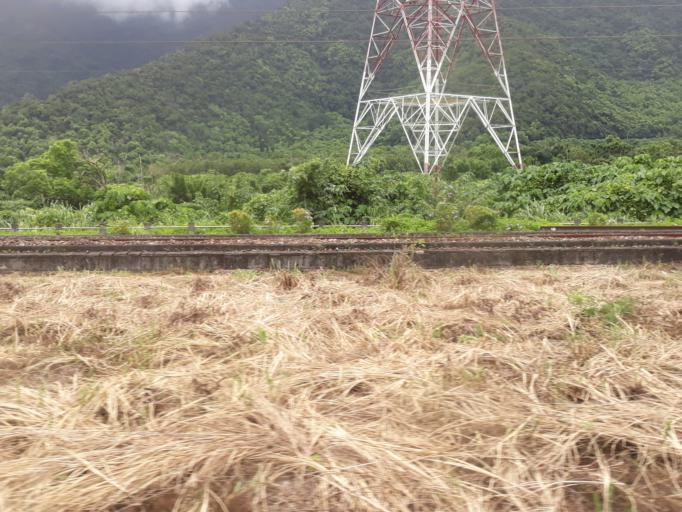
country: TW
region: Taiwan
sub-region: Yilan
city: Yilan
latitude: 24.4624
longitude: 121.8118
